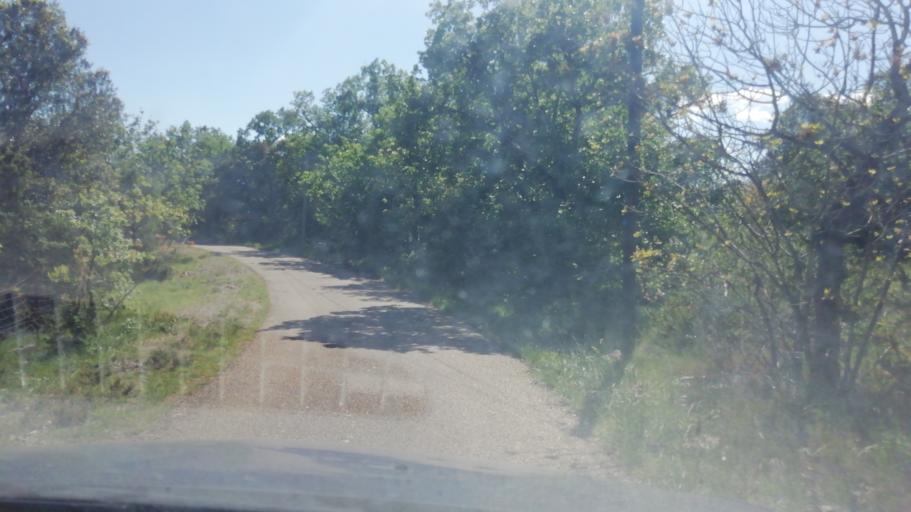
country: FR
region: Languedoc-Roussillon
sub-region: Departement de l'Herault
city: Saint-Mathieu-de-Treviers
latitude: 43.8278
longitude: 3.8139
